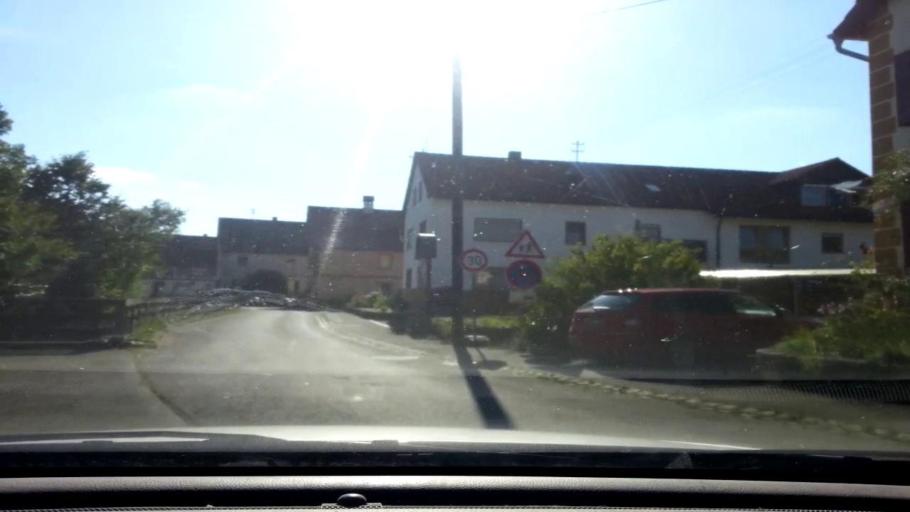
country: DE
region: Bavaria
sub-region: Upper Franconia
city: Schesslitz
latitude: 49.9642
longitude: 10.9995
